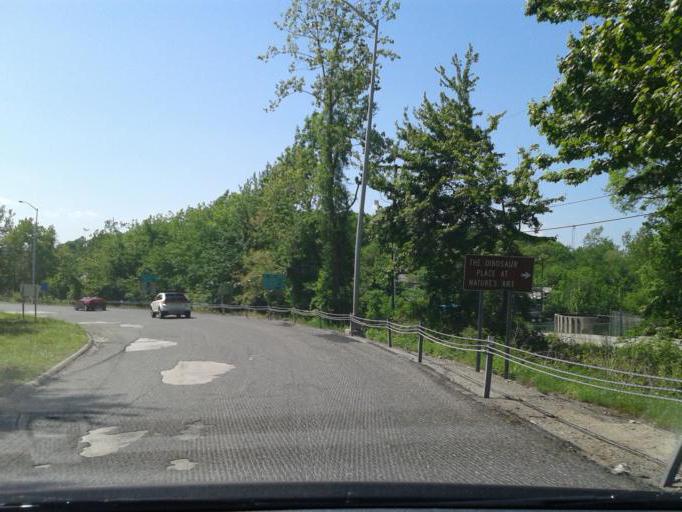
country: US
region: Connecticut
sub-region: New London County
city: Central Waterford
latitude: 41.3714
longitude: -72.1328
